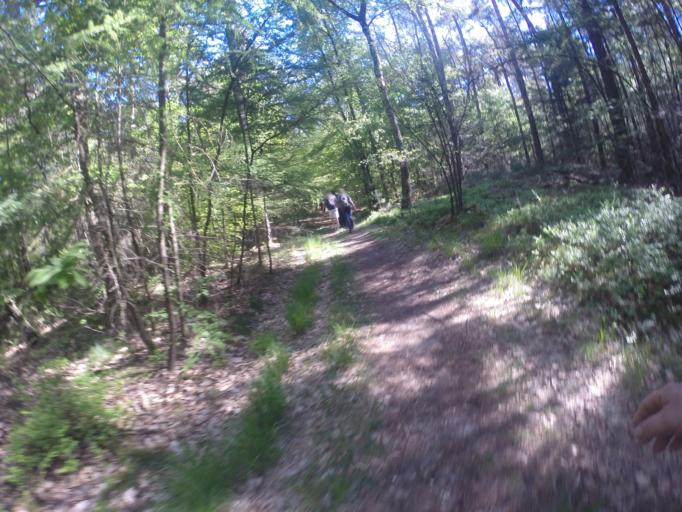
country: NL
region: Gelderland
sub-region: Gemeente Montferland
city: s-Heerenberg
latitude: 51.9166
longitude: 6.2341
